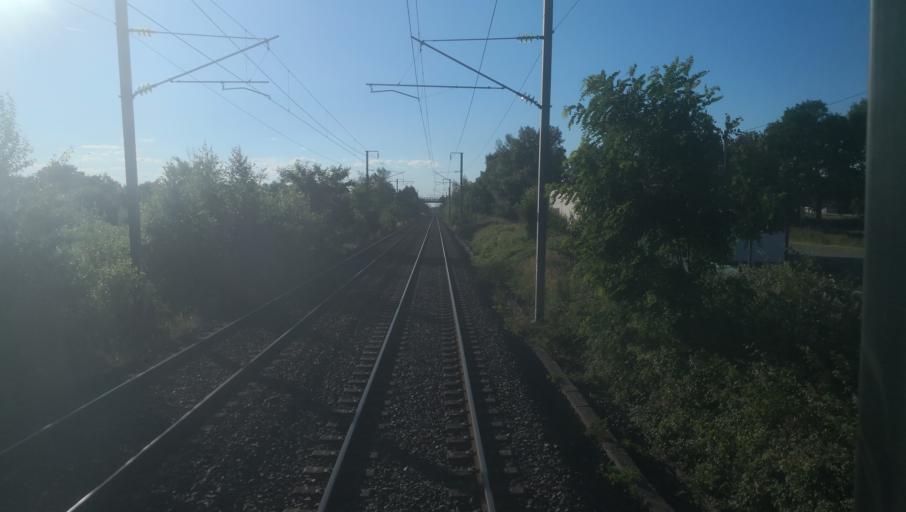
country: FR
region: Auvergne
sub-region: Departement de l'Allier
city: Avermes
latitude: 46.5953
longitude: 3.3101
